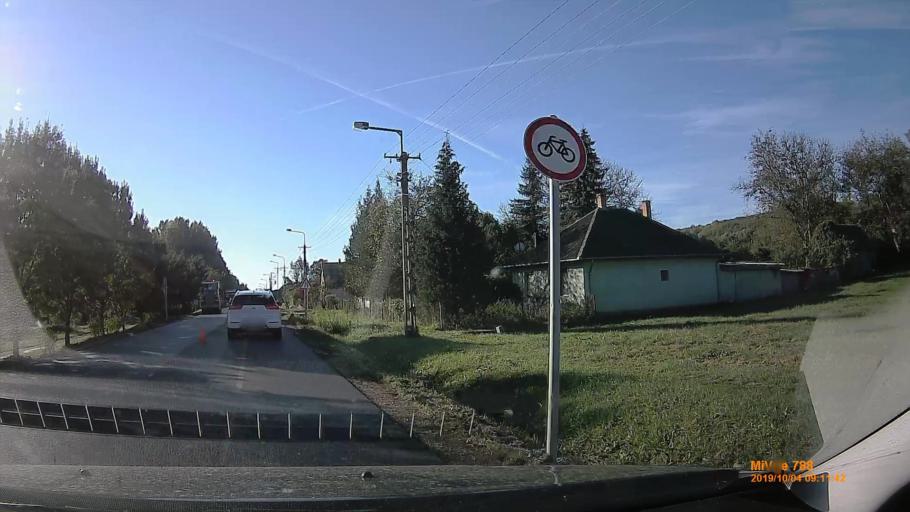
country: HU
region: Somogy
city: Karad
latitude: 46.6602
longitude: 17.7817
